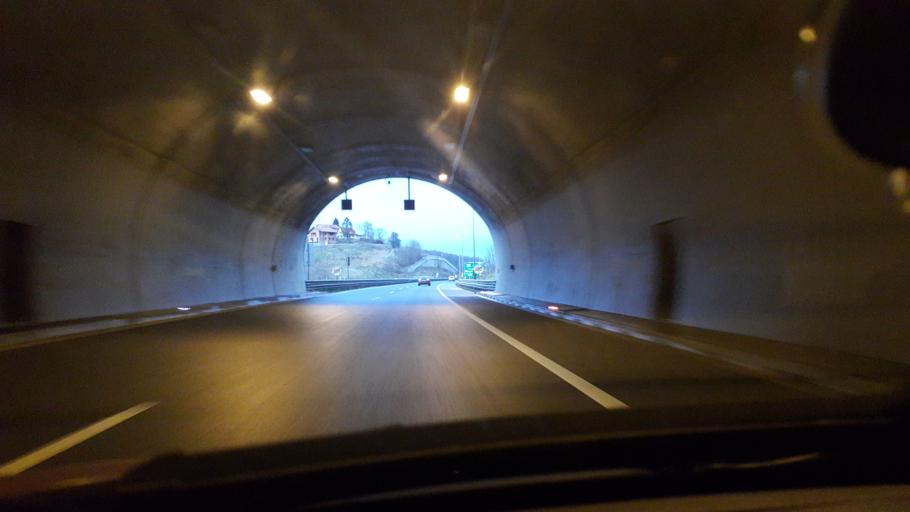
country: SI
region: Maribor
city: Maribor
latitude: 46.5665
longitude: 15.6858
